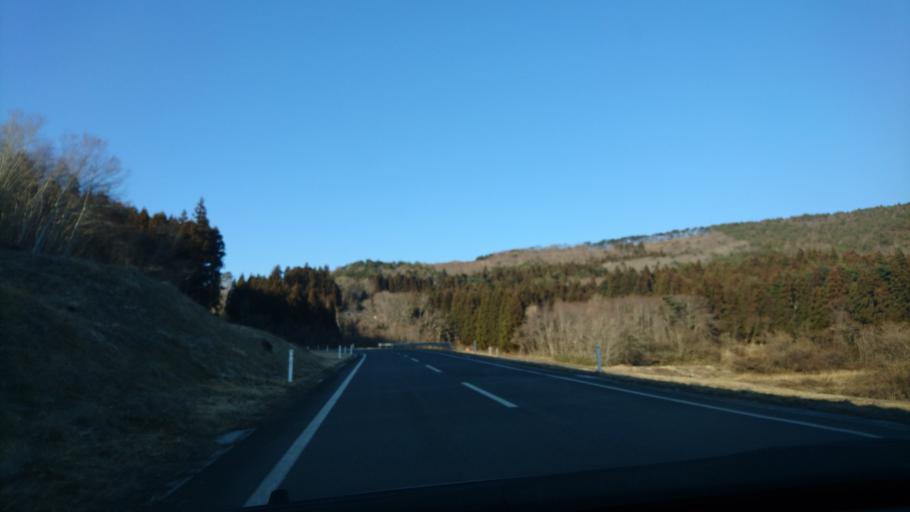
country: JP
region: Iwate
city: Ichinoseki
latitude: 38.8573
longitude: 141.3914
